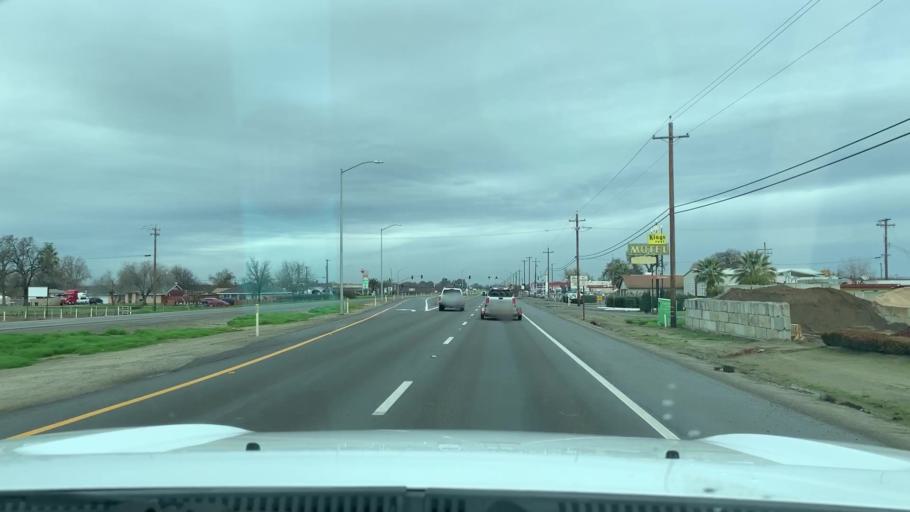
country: US
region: California
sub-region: Kings County
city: Lemoore
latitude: 36.3398
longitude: -119.8079
